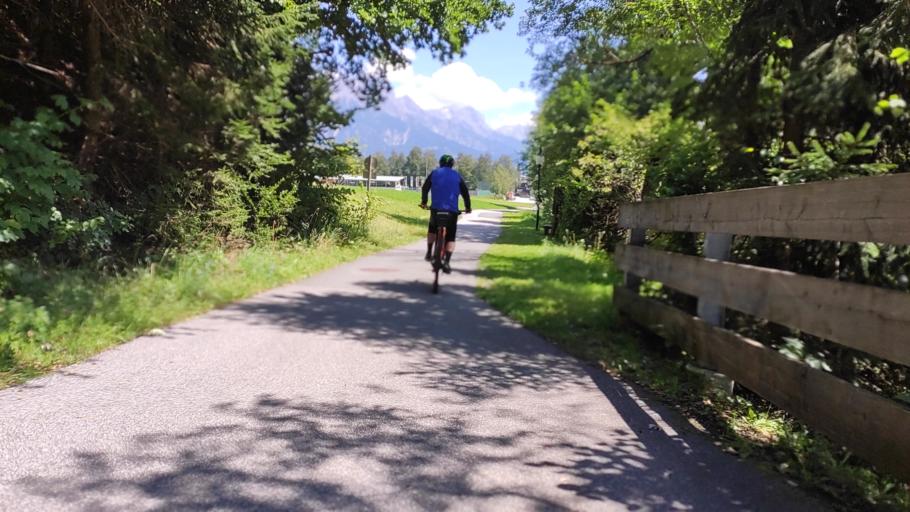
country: AT
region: Salzburg
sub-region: Politischer Bezirk Zell am See
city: Leogang
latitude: 47.4409
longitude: 12.7593
